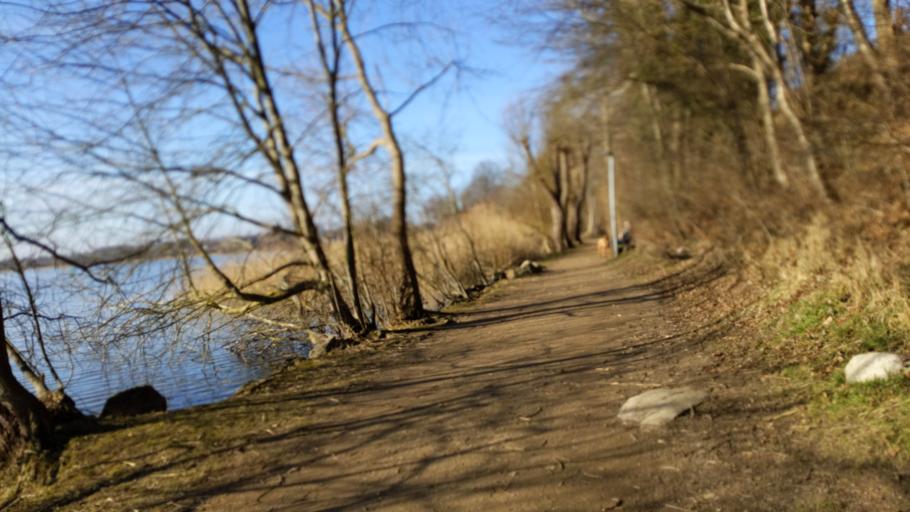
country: DE
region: Schleswig-Holstein
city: Susel
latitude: 54.0322
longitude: 10.7021
